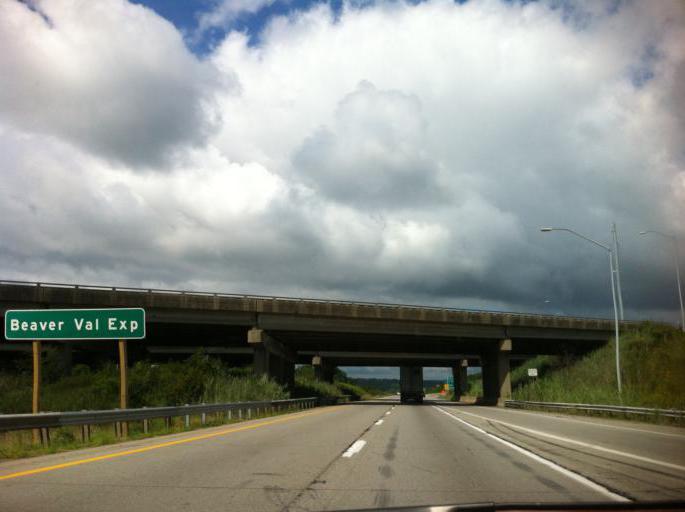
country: US
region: Pennsylvania
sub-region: Mercer County
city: Hermitage
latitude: 41.1849
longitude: -80.4429
